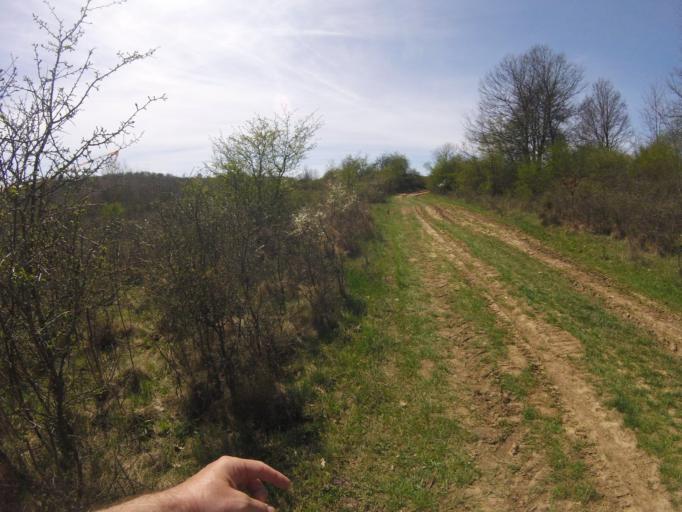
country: HU
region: Borsod-Abauj-Zemplen
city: Szendro
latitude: 48.4193
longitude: 20.7535
